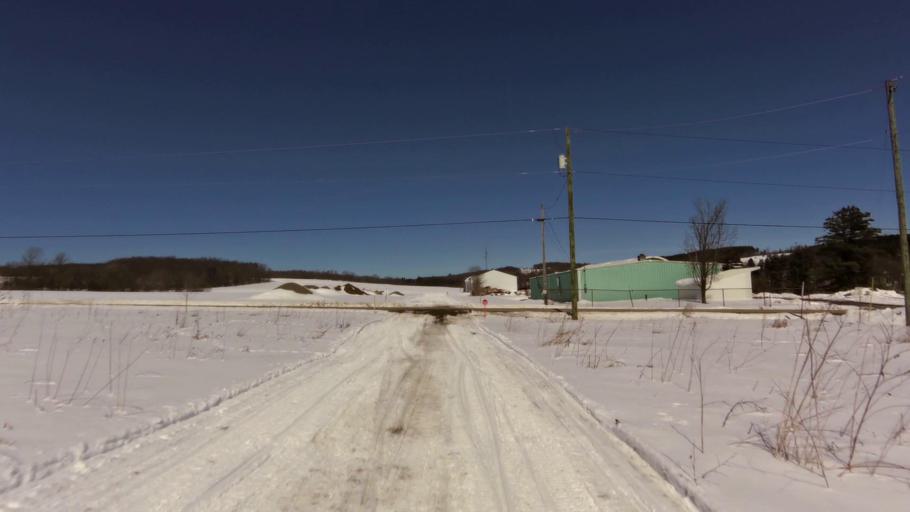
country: US
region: New York
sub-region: Allegany County
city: Houghton
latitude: 42.3920
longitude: -78.2587
